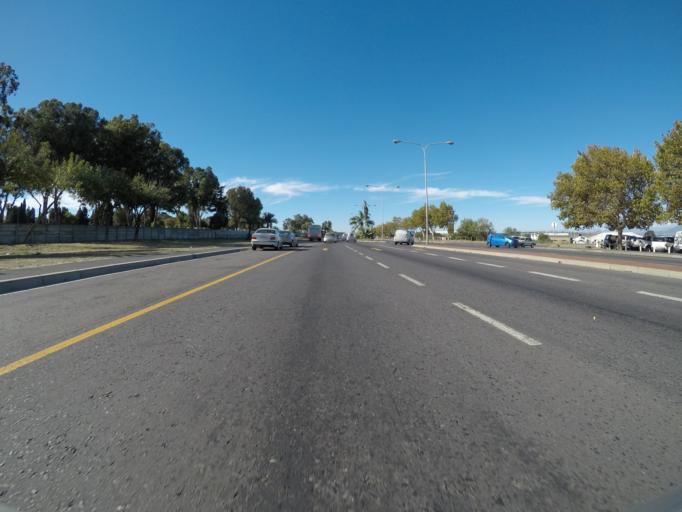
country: ZA
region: Western Cape
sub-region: City of Cape Town
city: Kraaifontein
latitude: -33.9099
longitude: 18.6658
